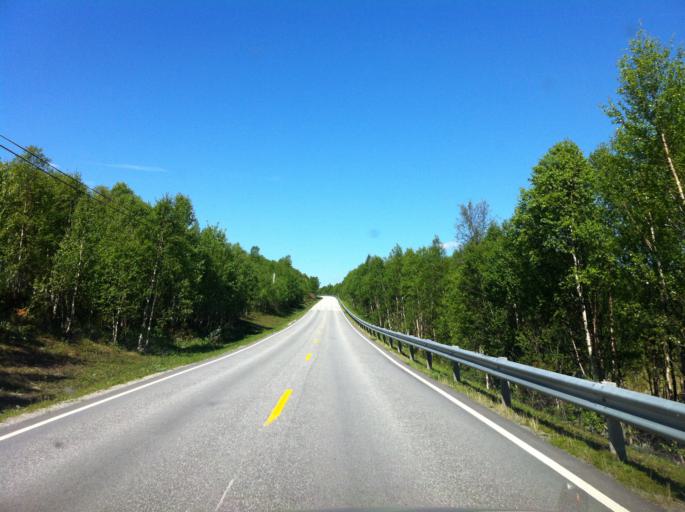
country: NO
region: Sor-Trondelag
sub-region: Roros
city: Roros
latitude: 62.5959
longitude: 11.7547
